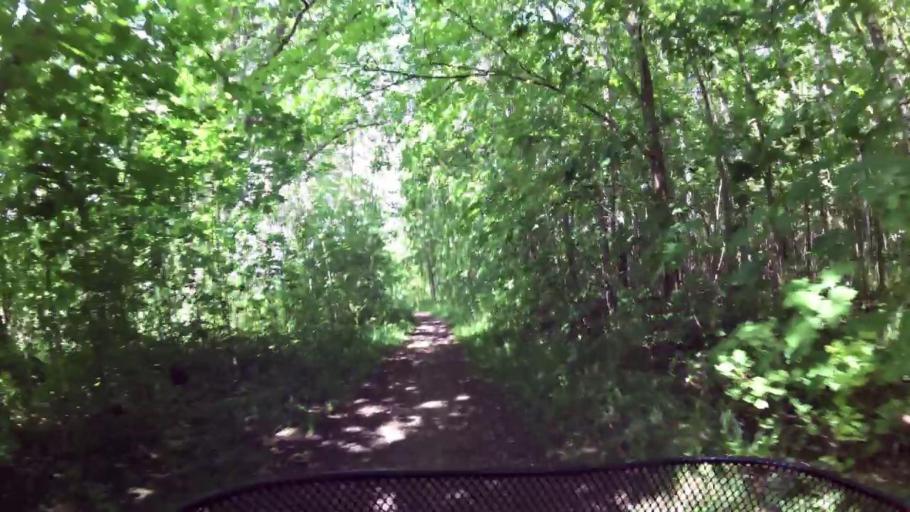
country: SE
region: OEstergoetland
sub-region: Linkopings Kommun
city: Malmslatt
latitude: 58.4218
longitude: 15.5195
